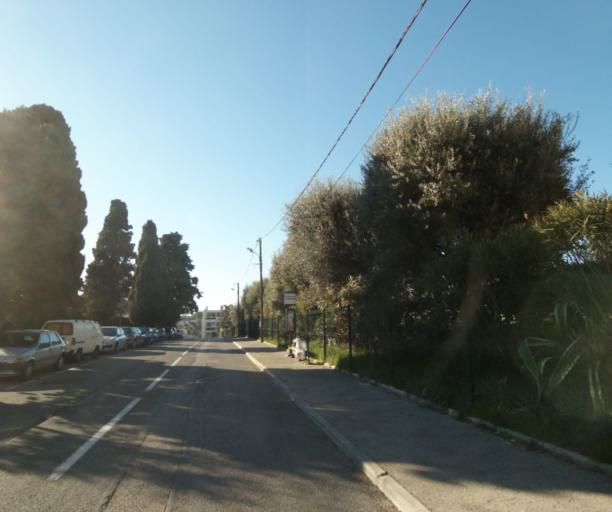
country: FR
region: Provence-Alpes-Cote d'Azur
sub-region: Departement des Alpes-Maritimes
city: Antibes
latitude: 43.5859
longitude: 7.1013
